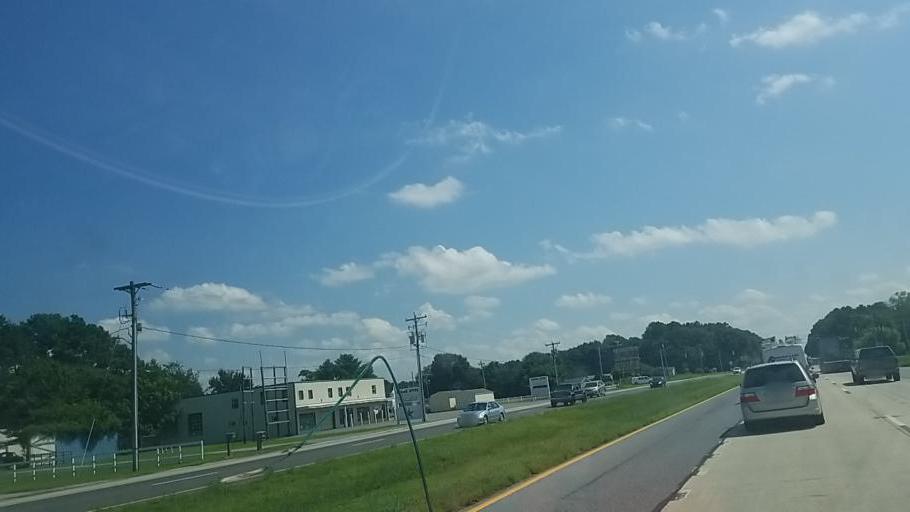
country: US
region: Delaware
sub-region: Sussex County
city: Milford
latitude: 38.8710
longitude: -75.4395
